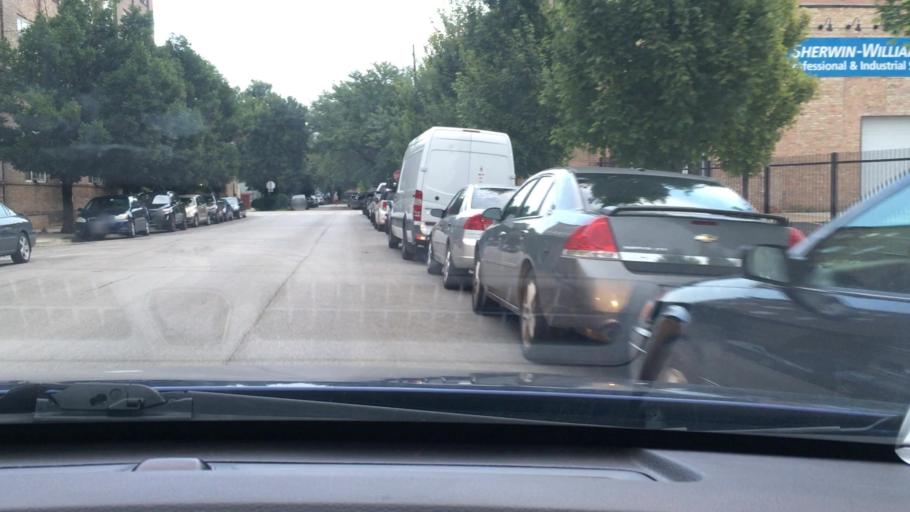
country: US
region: Illinois
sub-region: Cook County
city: Chicago
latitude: 41.8543
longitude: -87.6572
